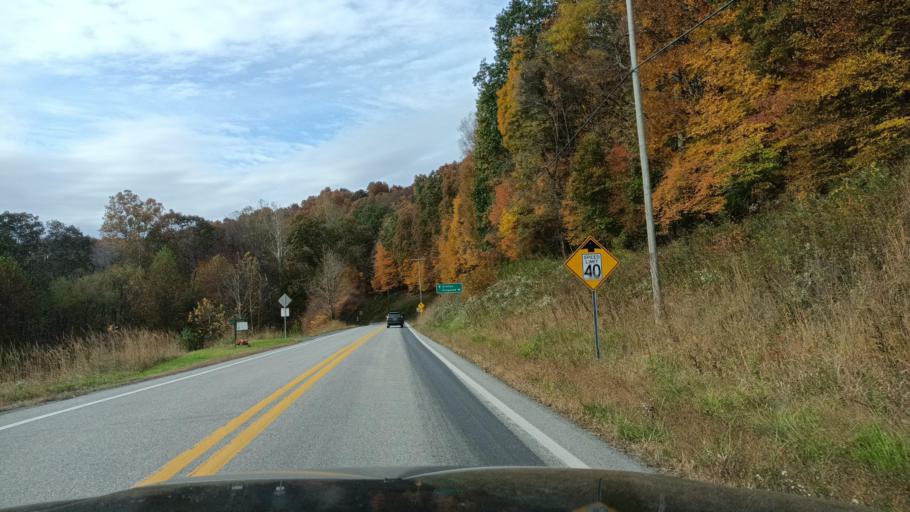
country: US
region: West Virginia
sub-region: Preston County
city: Kingwood
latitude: 39.3276
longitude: -79.8187
